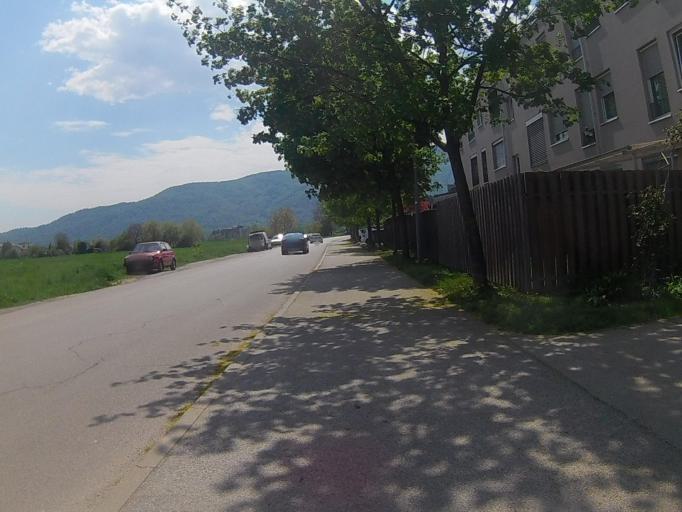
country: SI
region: Maribor
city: Pekre
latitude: 46.5532
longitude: 15.6151
